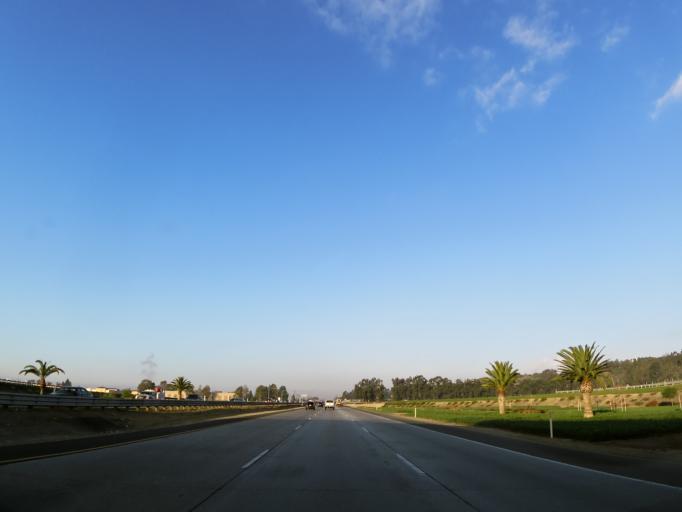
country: US
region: California
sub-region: Ventura County
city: Camarillo
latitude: 34.2205
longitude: -119.0855
